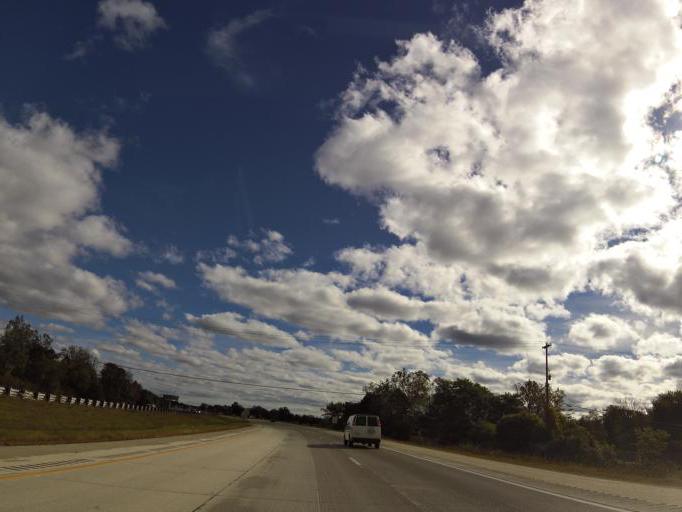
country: US
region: Michigan
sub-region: Genesee County
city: Burton
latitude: 43.0143
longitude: -83.6260
